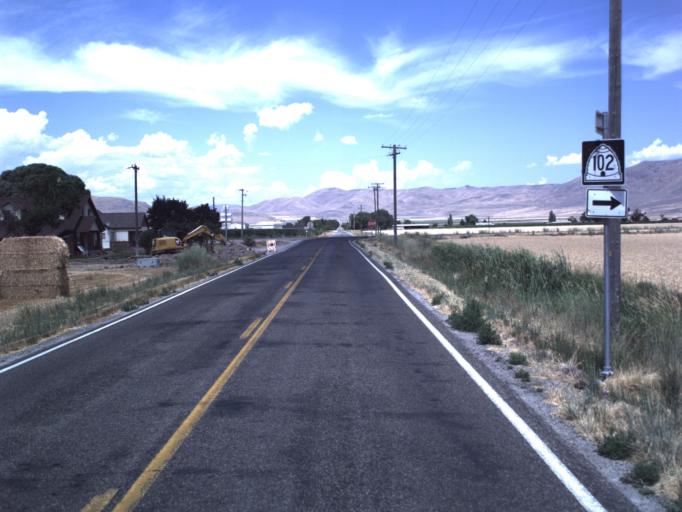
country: US
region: Utah
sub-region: Box Elder County
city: Tremonton
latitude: 41.7079
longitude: -112.2781
